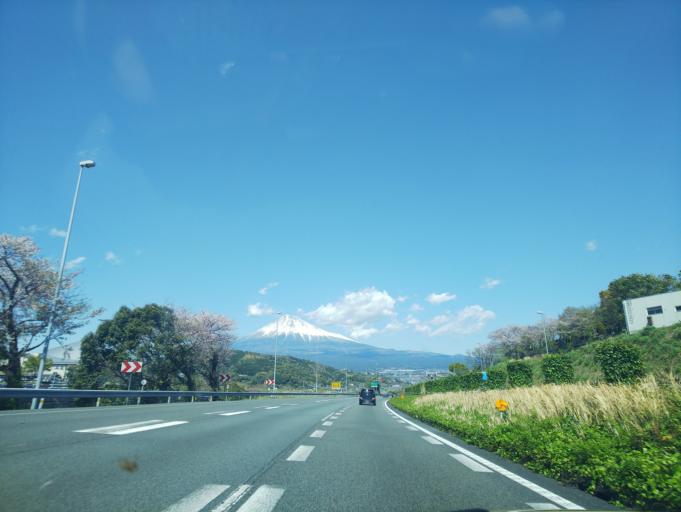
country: JP
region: Shizuoka
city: Fujinomiya
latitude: 35.1594
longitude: 138.6187
